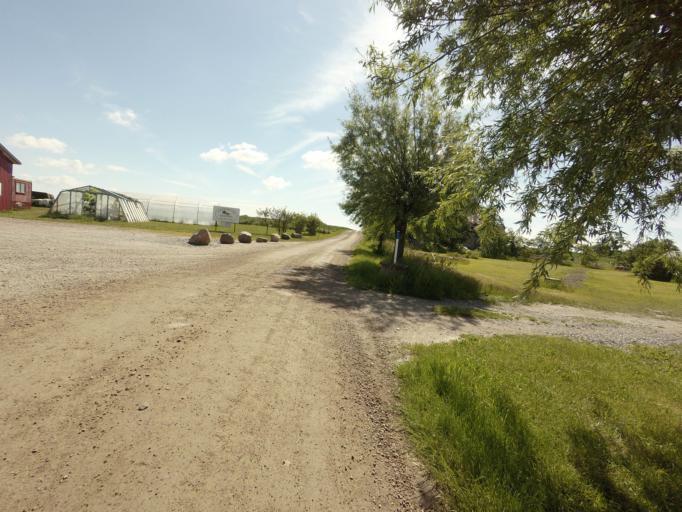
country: SE
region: Skane
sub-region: Trelleborgs Kommun
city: Skare
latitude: 55.4184
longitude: 13.0322
